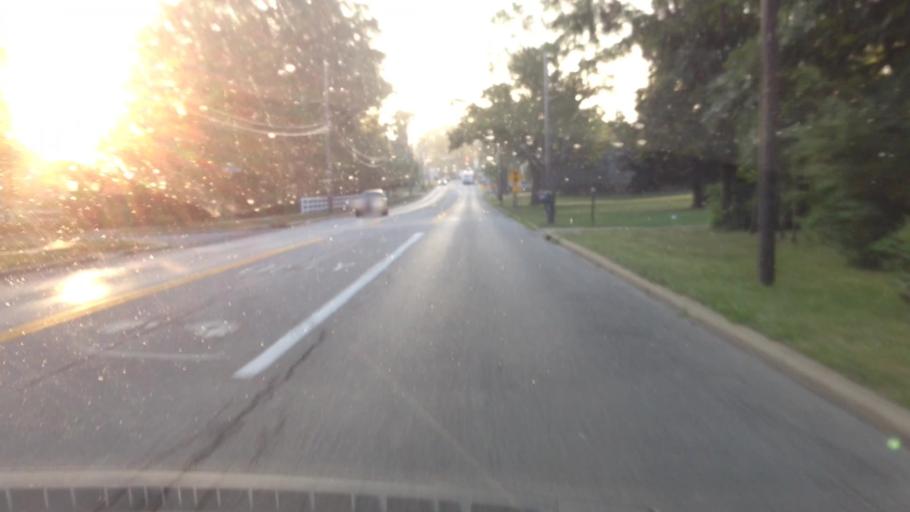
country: US
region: Ohio
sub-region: Summit County
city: Cuyahoga Falls
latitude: 41.1588
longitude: -81.4959
